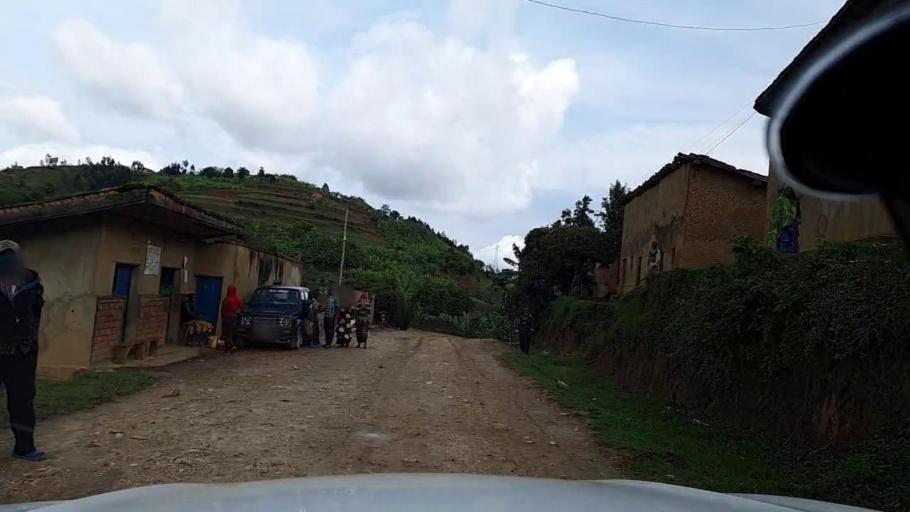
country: RW
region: Western Province
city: Kibuye
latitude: -2.1478
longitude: 29.5341
